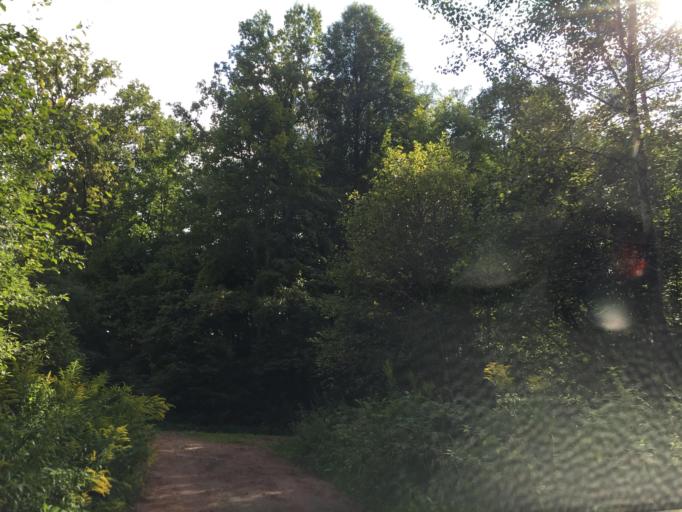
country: LV
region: Priekuli
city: Priekuli
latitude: 57.3545
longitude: 25.3294
